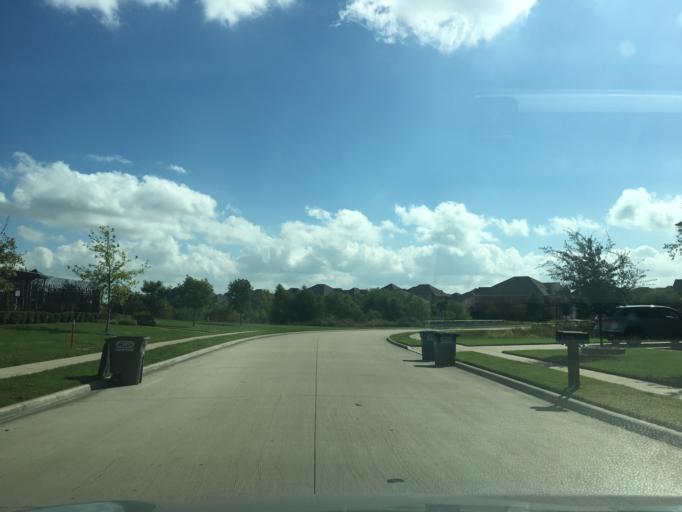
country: US
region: Texas
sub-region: Dallas County
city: Sachse
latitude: 32.9596
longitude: -96.5756
